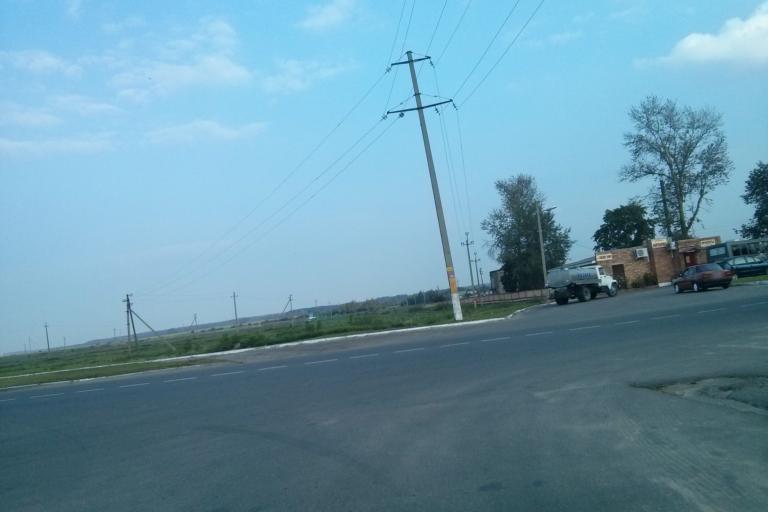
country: BY
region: Minsk
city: Chervyen'
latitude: 53.7206
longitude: 28.4188
